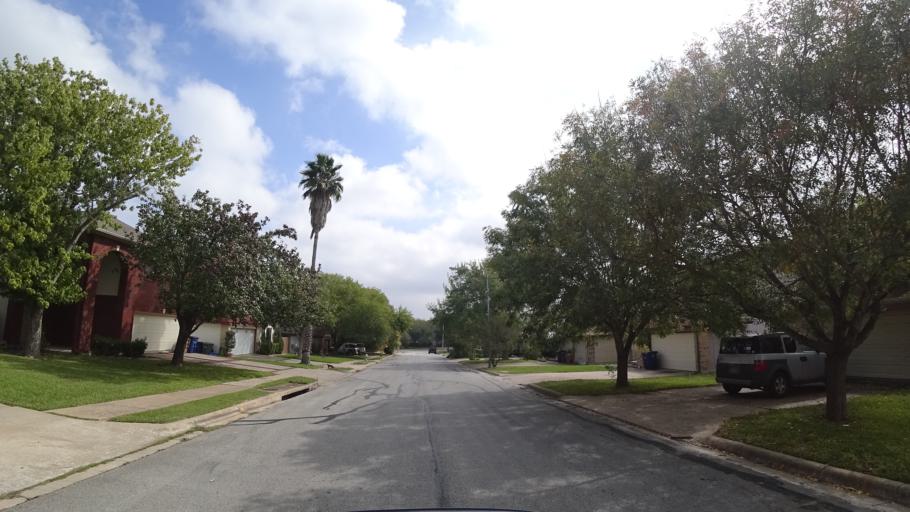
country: US
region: Texas
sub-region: Travis County
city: Shady Hollow
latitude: 30.1970
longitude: -97.8301
